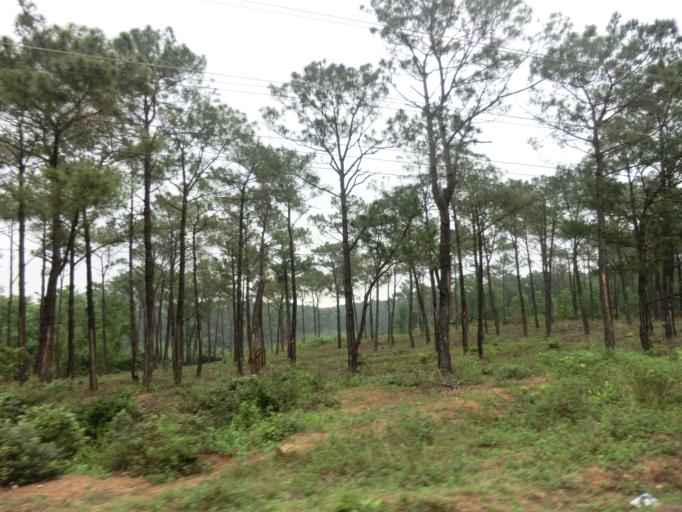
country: VN
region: Quang Binh
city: Ba Don
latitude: 17.6616
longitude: 106.4323
